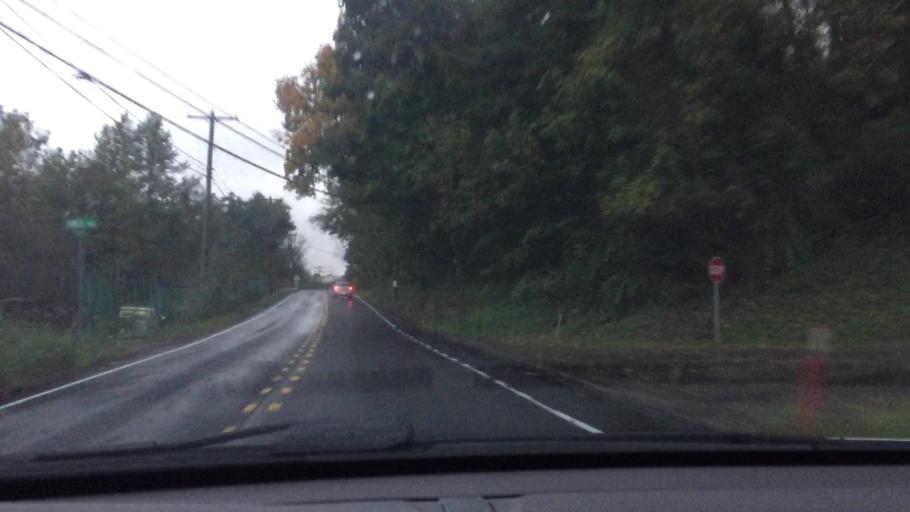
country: US
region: Pennsylvania
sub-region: Washington County
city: Bentleyville
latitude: 40.1305
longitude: -80.0053
